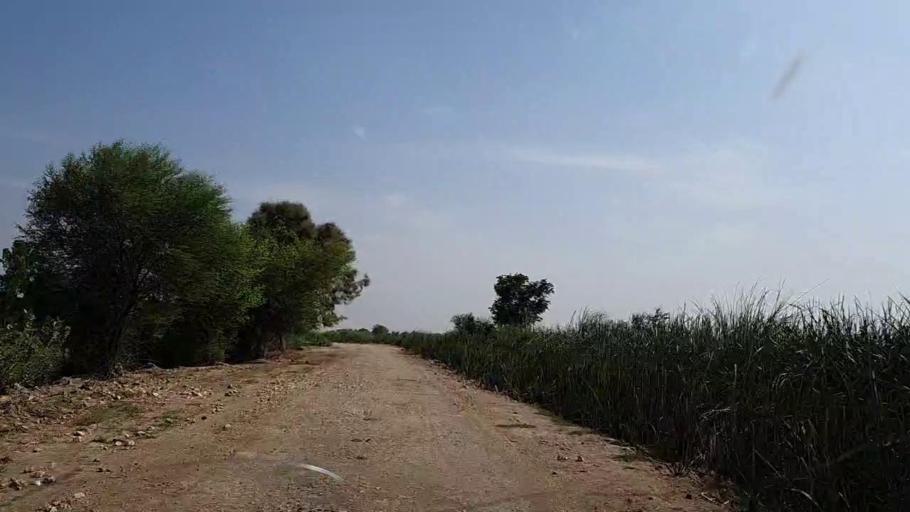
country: PK
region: Sindh
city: Khanpur
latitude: 27.7067
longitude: 69.3624
